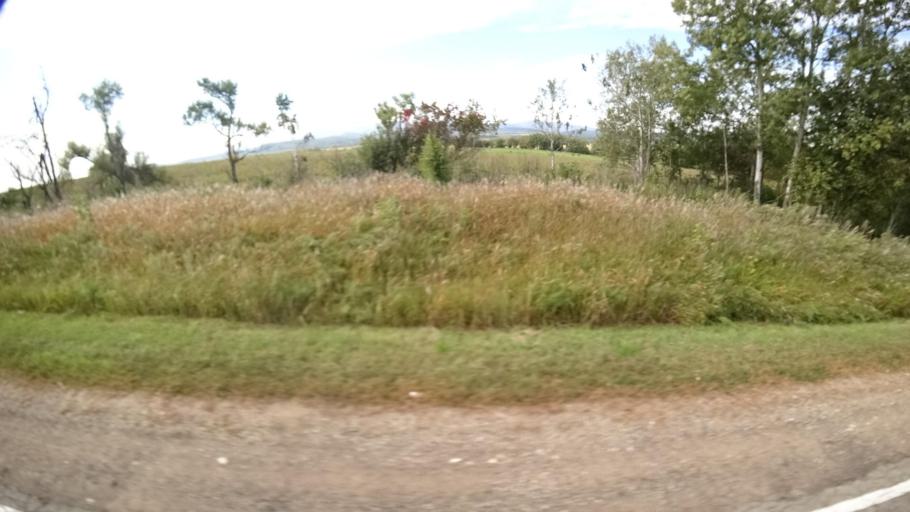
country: RU
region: Primorskiy
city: Dostoyevka
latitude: 44.3163
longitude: 133.4651
